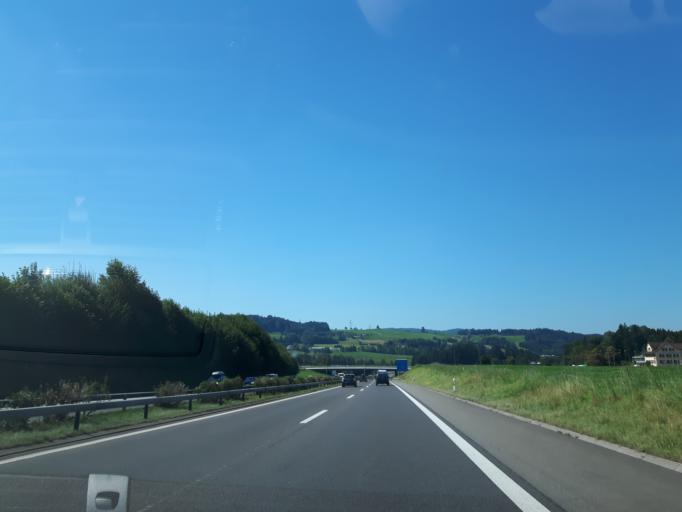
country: CH
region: Zurich
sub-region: Bezirk Horgen
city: Au
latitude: 47.2303
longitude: 8.6380
